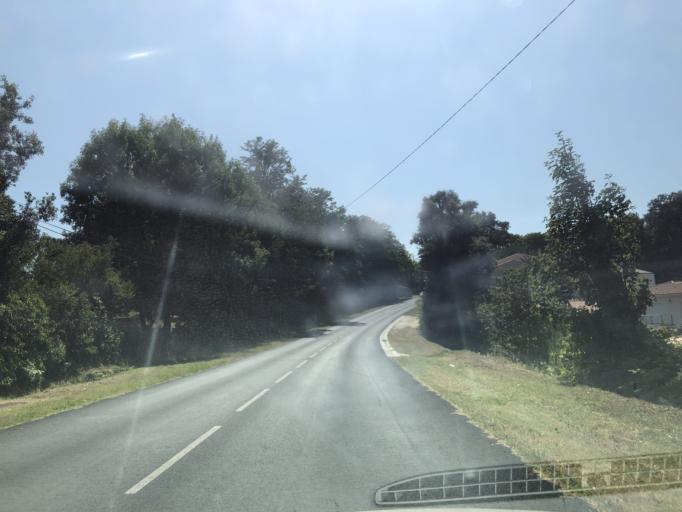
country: FR
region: Poitou-Charentes
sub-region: Departement de la Charente-Maritime
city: Meschers-sur-Gironde
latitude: 45.5634
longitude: -0.9659
